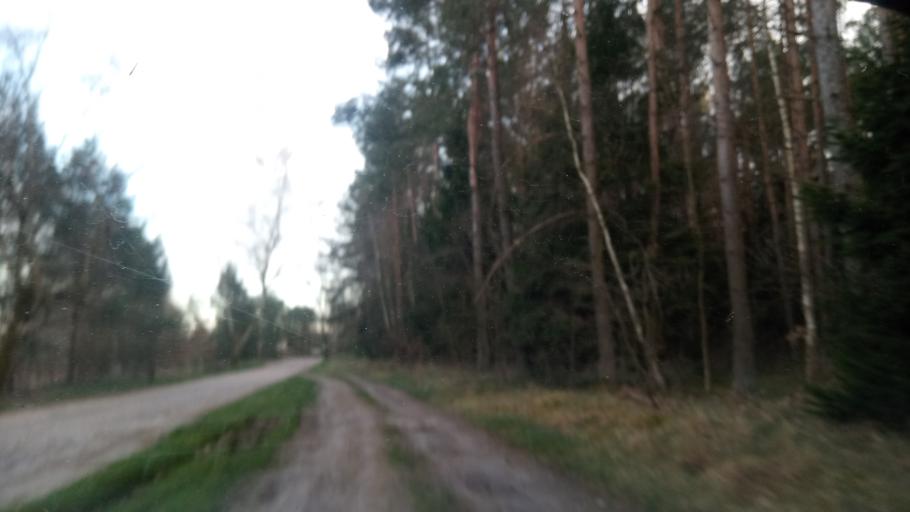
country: PL
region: West Pomeranian Voivodeship
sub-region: Powiat szczecinecki
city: Lubowo
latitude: 53.5561
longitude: 16.3879
